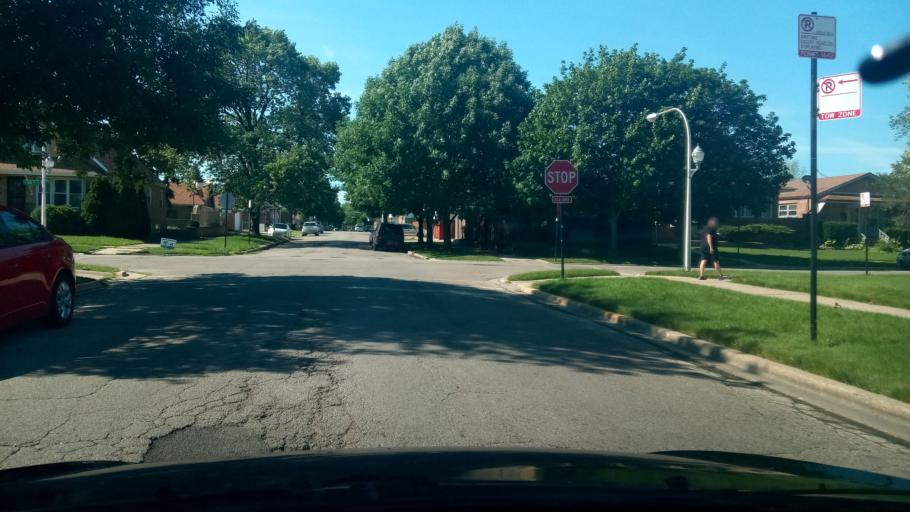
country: US
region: Illinois
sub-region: Cook County
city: Hometown
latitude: 41.7691
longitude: -87.7198
